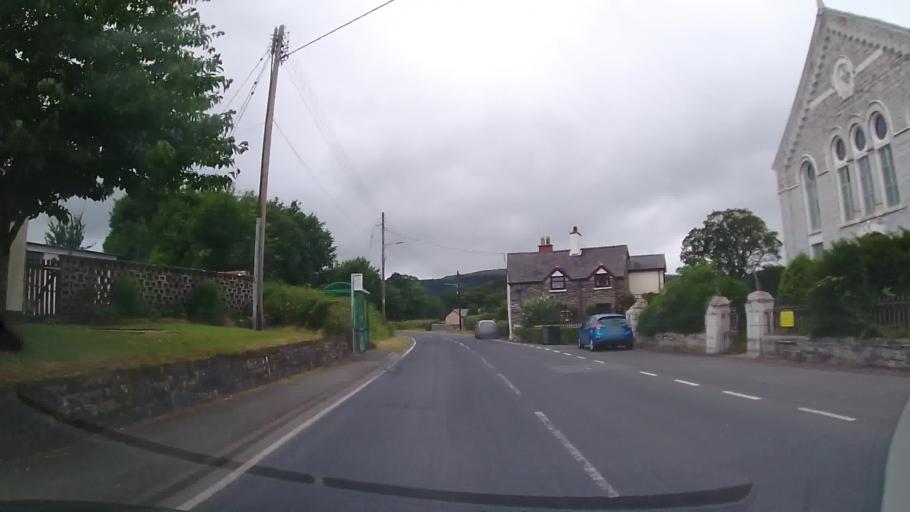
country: GB
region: Wales
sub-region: Denbighshire
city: Llandrillo
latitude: 52.9228
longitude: -3.4393
